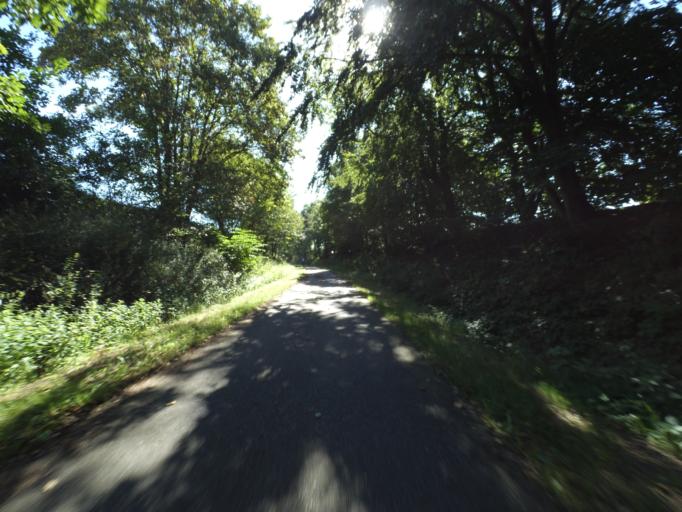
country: DE
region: Rheinland-Pfalz
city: Pantenburg
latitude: 50.0979
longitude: 6.8425
